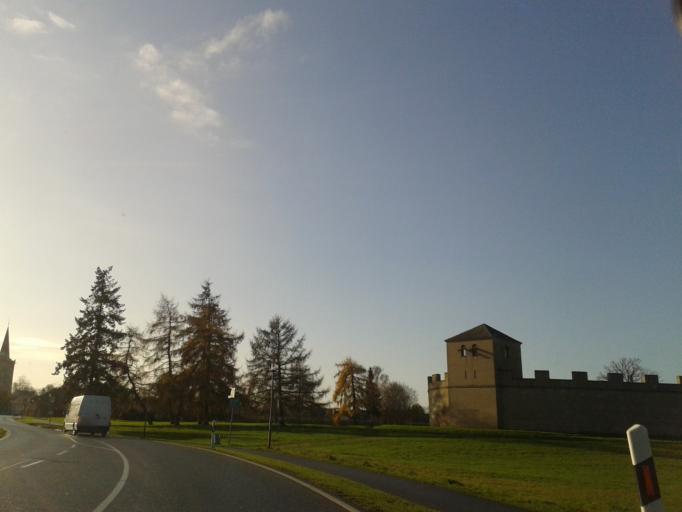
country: DE
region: North Rhine-Westphalia
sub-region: Regierungsbezirk Dusseldorf
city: Xanten
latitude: 51.6680
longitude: 6.4537
